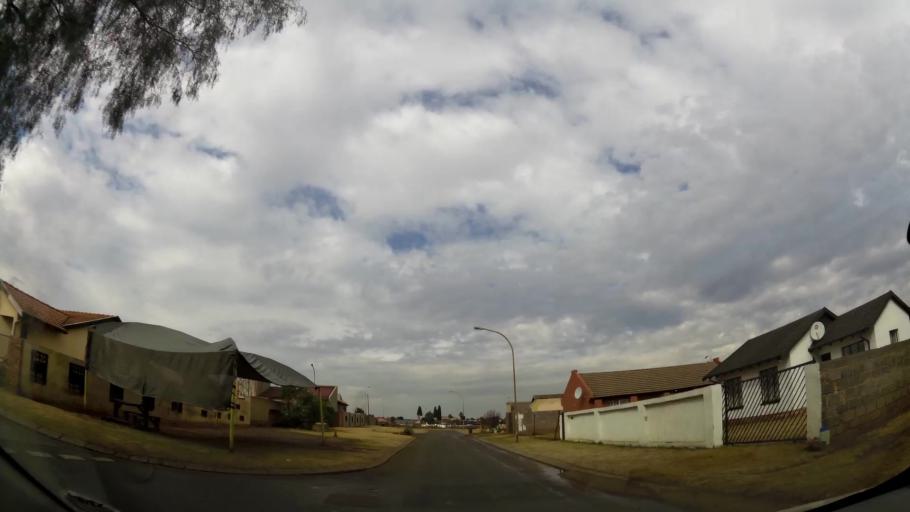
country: ZA
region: Gauteng
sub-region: Ekurhuleni Metropolitan Municipality
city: Germiston
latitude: -26.3239
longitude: 28.1761
